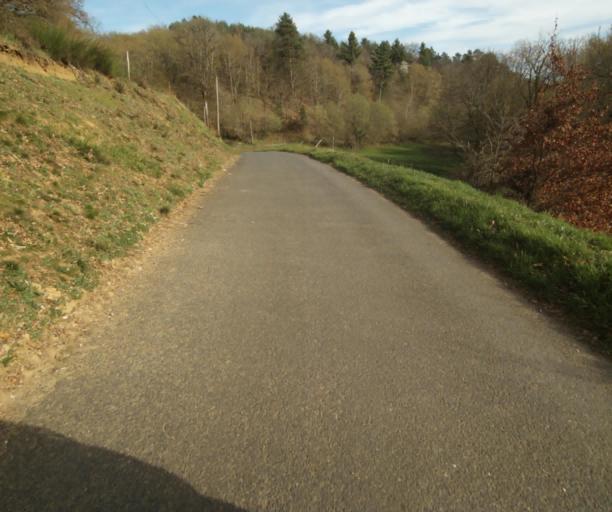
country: FR
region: Limousin
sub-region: Departement de la Correze
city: Naves
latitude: 45.2952
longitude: 1.7570
